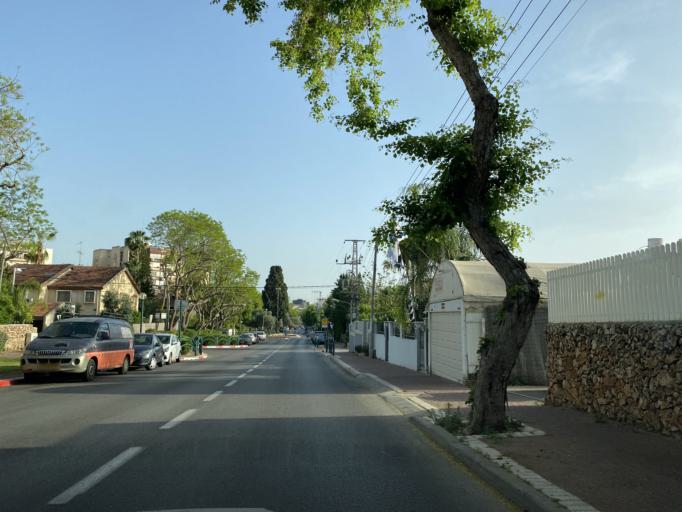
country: IL
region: Central District
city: Kfar Saba
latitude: 32.1821
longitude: 34.9102
